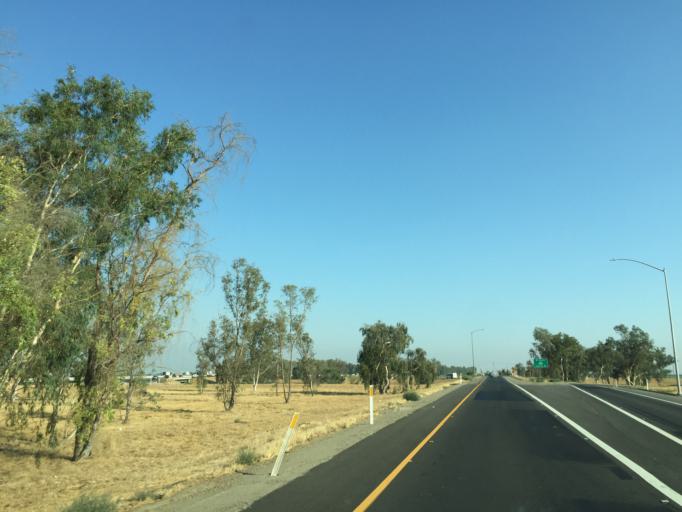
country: US
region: California
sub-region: Tulare County
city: Goshen
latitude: 36.3309
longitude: -119.4118
